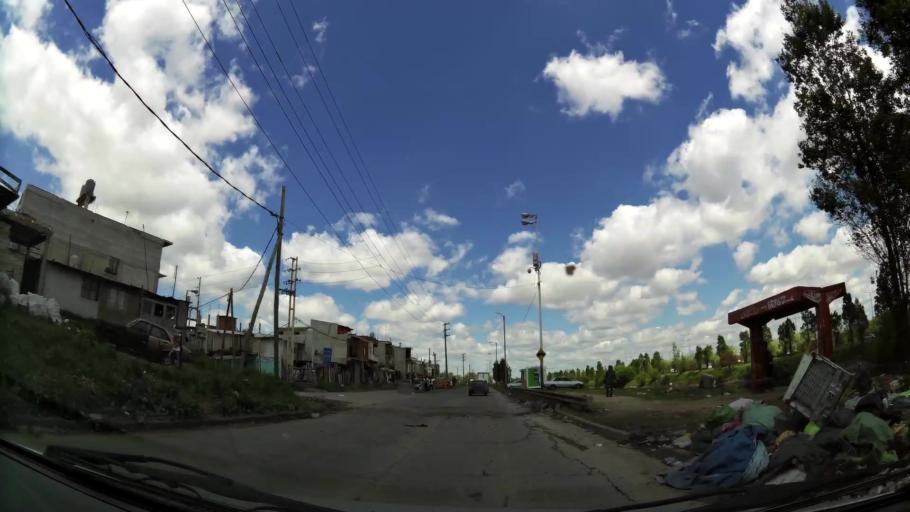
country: AR
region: Buenos Aires F.D.
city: Villa Lugano
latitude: -34.6889
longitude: -58.4464
